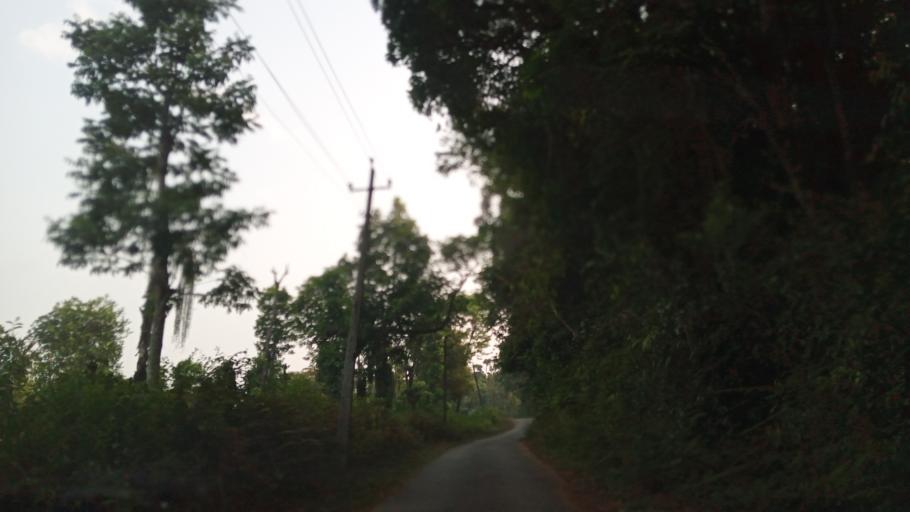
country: IN
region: Karnataka
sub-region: Chikmagalur
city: Mudigere
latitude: 13.0003
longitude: 75.6233
